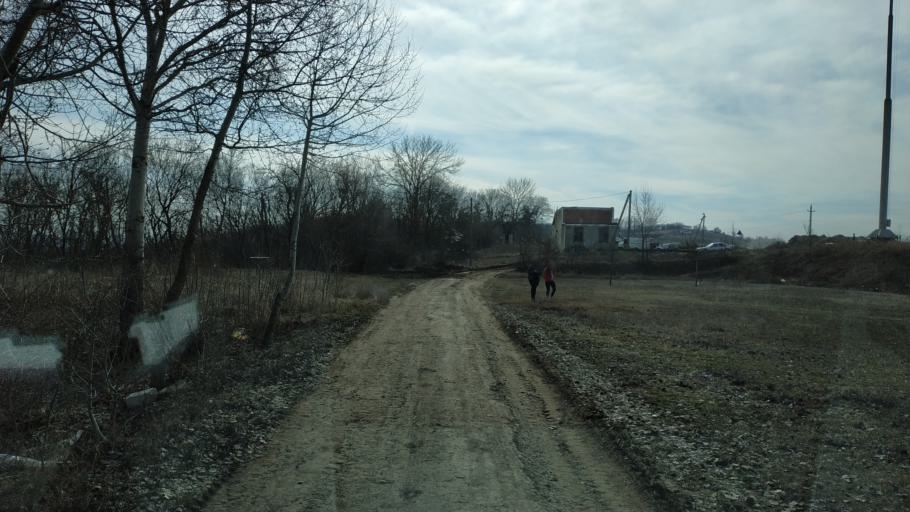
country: MD
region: Nisporeni
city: Nisporeni
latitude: 47.1934
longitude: 28.0669
